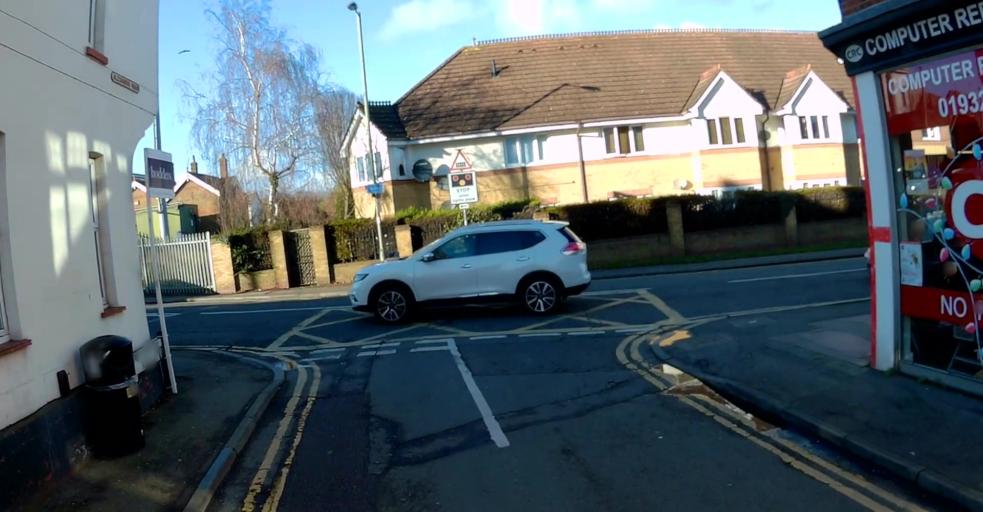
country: GB
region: England
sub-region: Surrey
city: Addlestone
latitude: 51.3729
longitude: -0.4835
